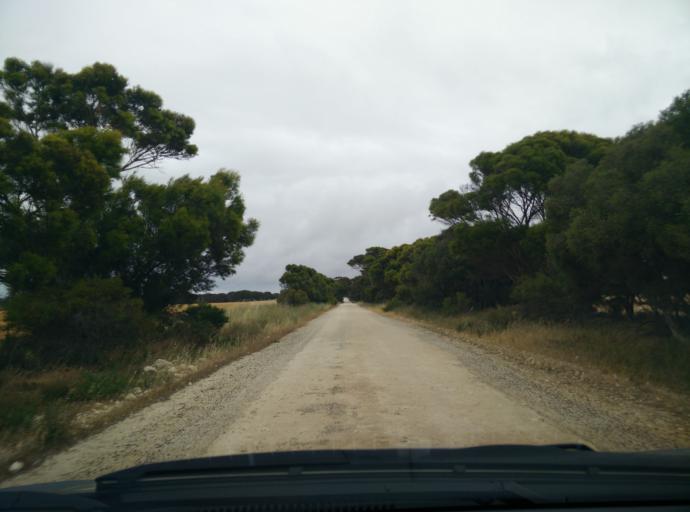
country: AU
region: South Australia
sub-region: Kangaroo Island
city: Kingscote
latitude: -35.8693
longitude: 137.5244
